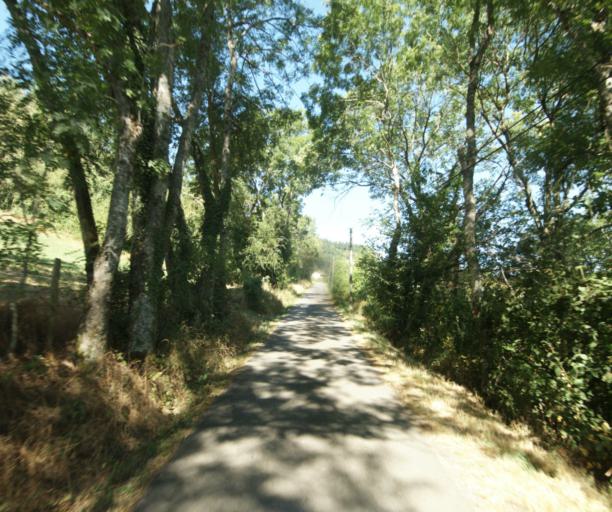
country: FR
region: Rhone-Alpes
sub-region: Departement du Rhone
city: Saint-Romain-de-Popey
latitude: 45.8108
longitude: 4.5104
